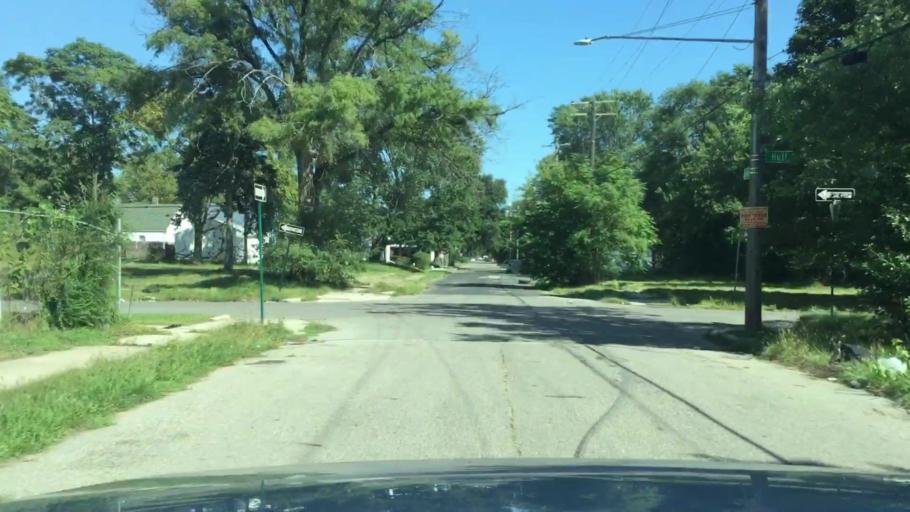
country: US
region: Michigan
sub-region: Wayne County
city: Highland Park
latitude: 42.4281
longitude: -83.0891
